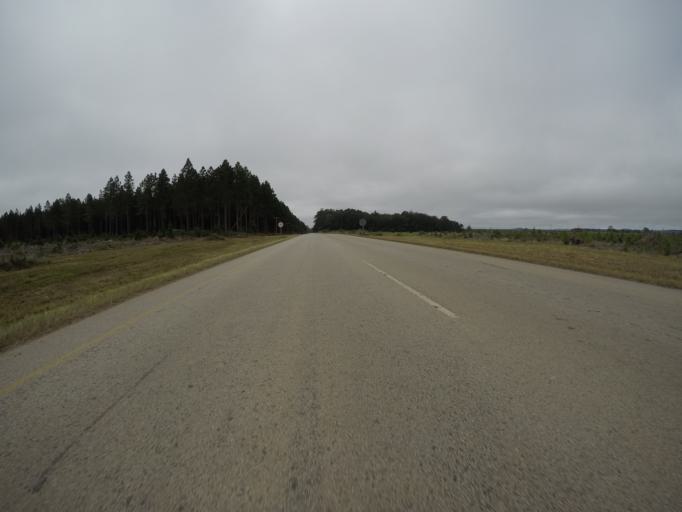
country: ZA
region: Eastern Cape
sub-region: Cacadu District Municipality
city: Kareedouw
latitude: -33.9940
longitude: 24.1046
